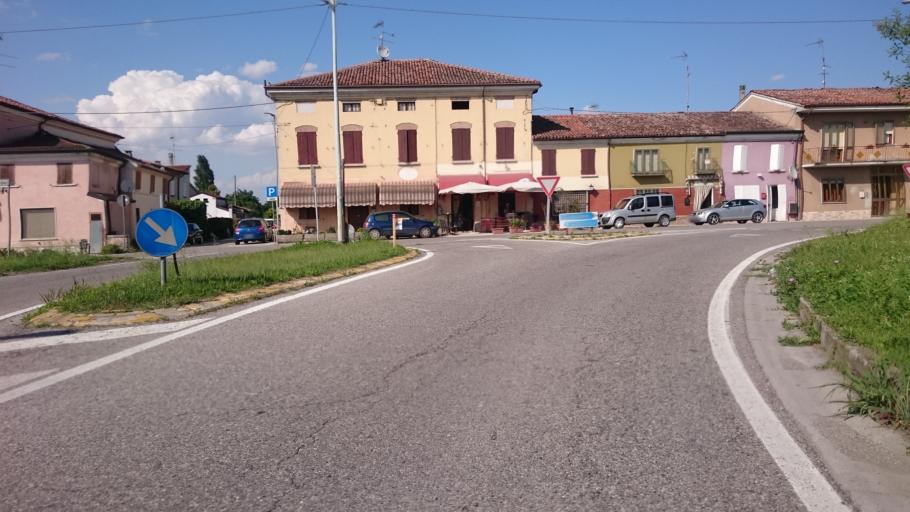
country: IT
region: Lombardy
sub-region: Provincia di Mantova
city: Gazzo
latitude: 45.1601
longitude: 10.8936
